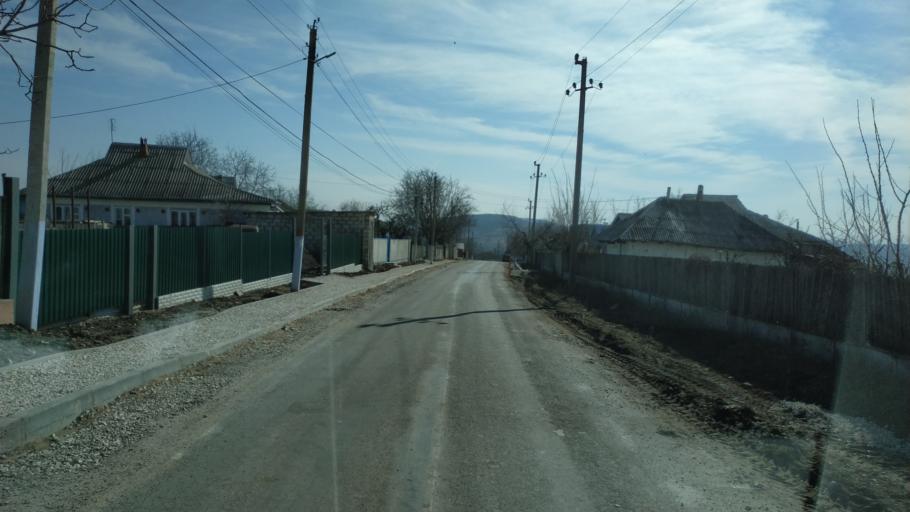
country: MD
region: Nisporeni
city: Nisporeni
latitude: 47.2017
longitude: 28.0610
